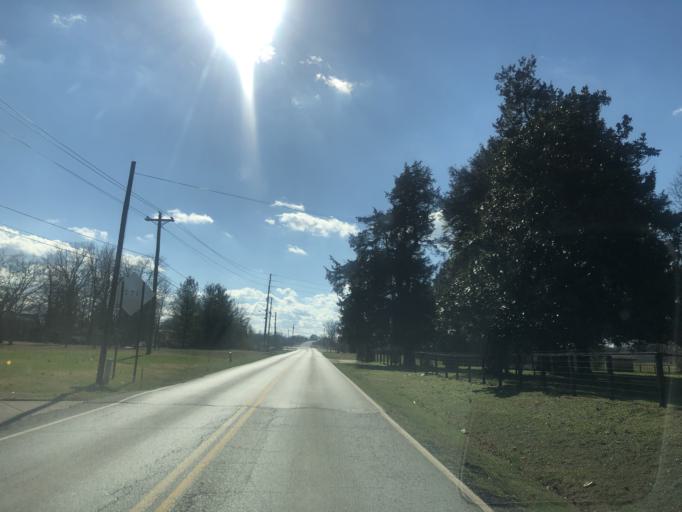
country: US
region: Tennessee
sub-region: Rutherford County
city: Smyrna
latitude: 35.8770
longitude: -86.4976
